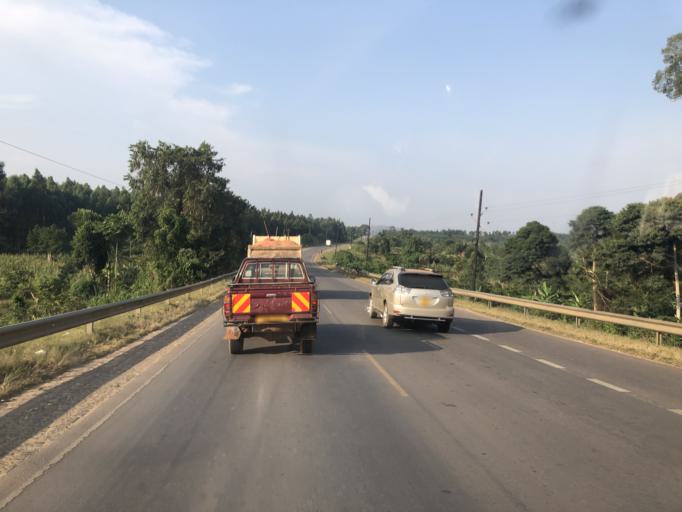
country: UG
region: Central Region
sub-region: Butambala District
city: Gombe
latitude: 0.0813
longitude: 32.1300
